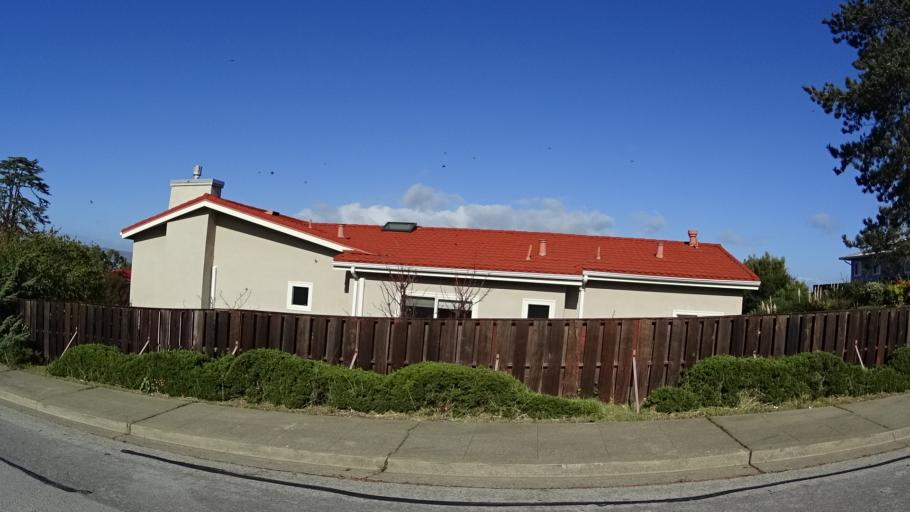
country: US
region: California
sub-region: San Mateo County
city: Hillsborough
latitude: 37.5811
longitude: -122.3944
